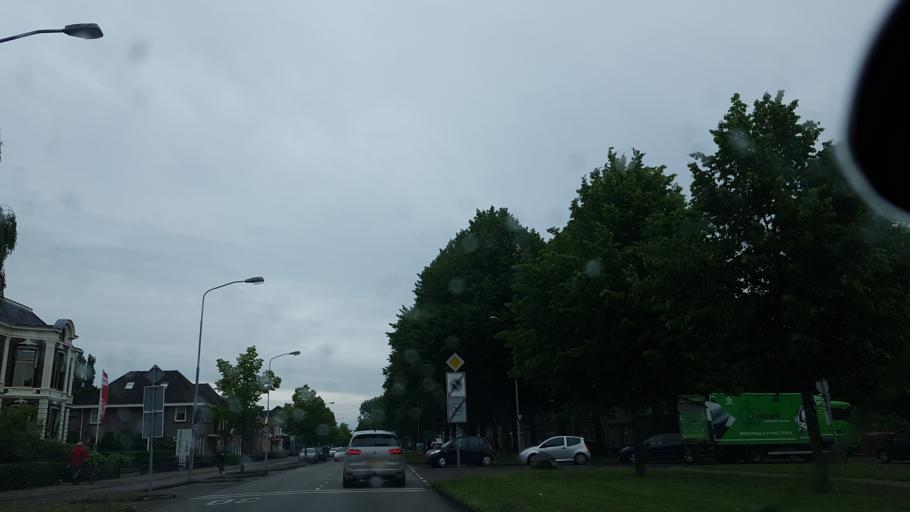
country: NL
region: Groningen
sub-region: Gemeente Hoogezand-Sappemeer
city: Hoogezand
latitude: 53.1633
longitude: 6.7448
